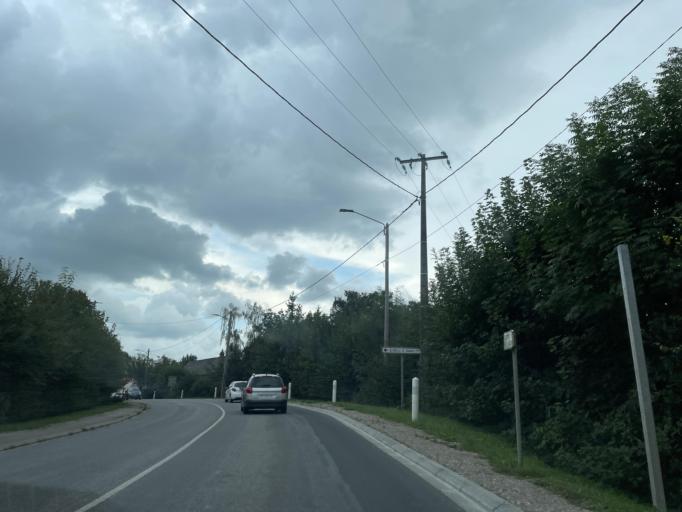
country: FR
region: Haute-Normandie
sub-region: Departement de la Seine-Maritime
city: Gournay-en-Bray
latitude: 49.4864
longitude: 1.6972
